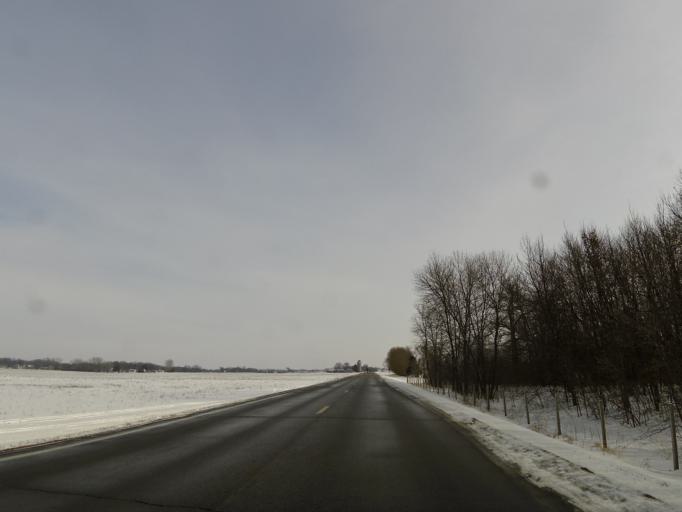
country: US
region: Minnesota
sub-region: McLeod County
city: Lester Prairie
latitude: 44.8766
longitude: -93.9820
